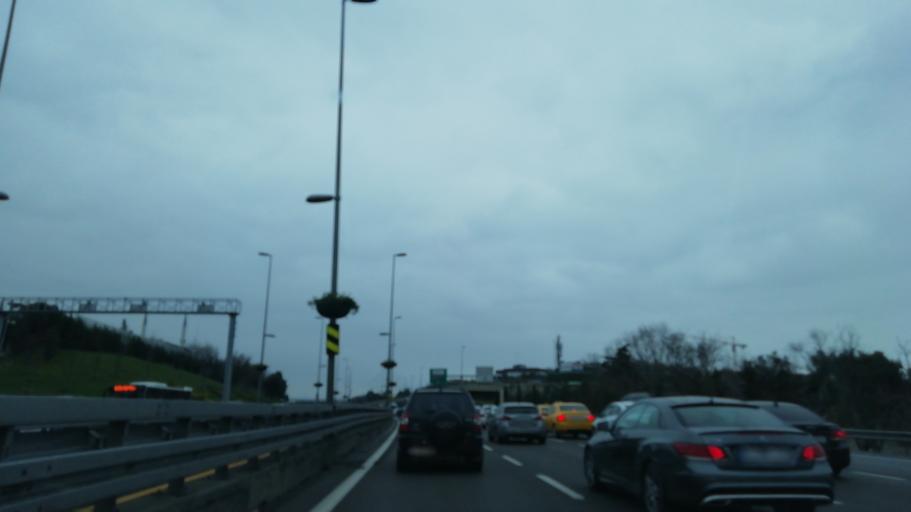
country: TR
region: Istanbul
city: UEskuedar
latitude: 41.0280
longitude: 29.0458
